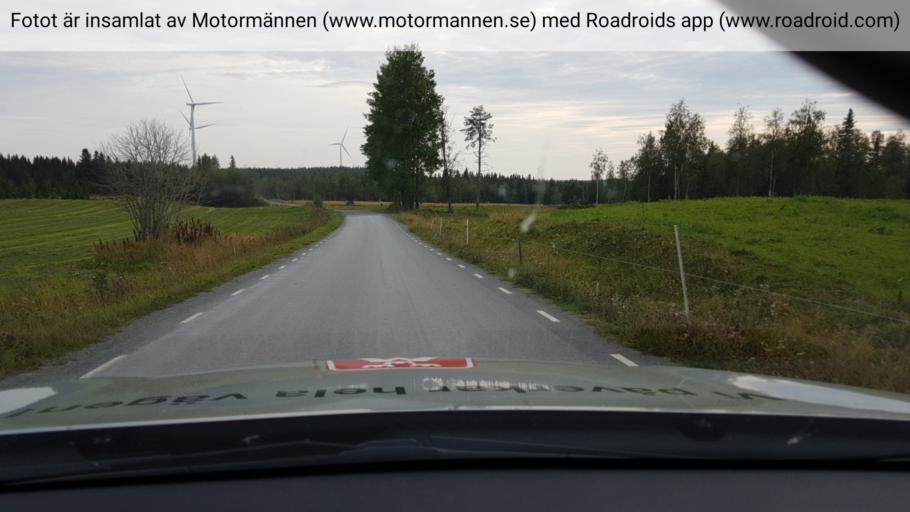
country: SE
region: Jaemtland
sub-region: OEstersunds Kommun
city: Lit
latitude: 63.6068
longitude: 14.9965
